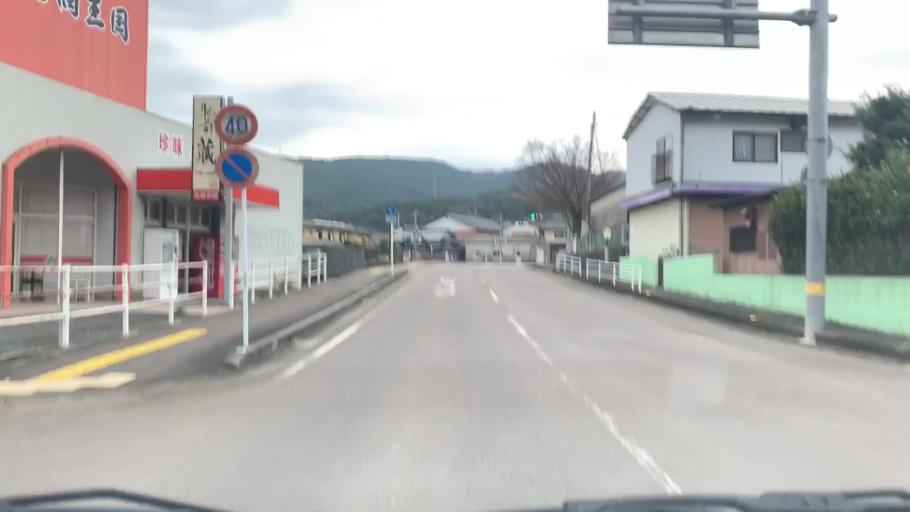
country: JP
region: Saga Prefecture
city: Ureshinomachi-shimojuku
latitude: 33.0917
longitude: 129.9766
